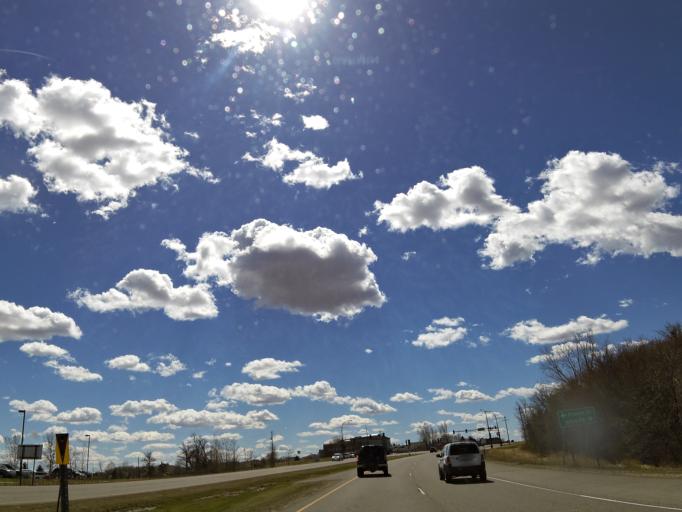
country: US
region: Minnesota
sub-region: Washington County
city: Woodbury
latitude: 44.9164
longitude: -92.9341
